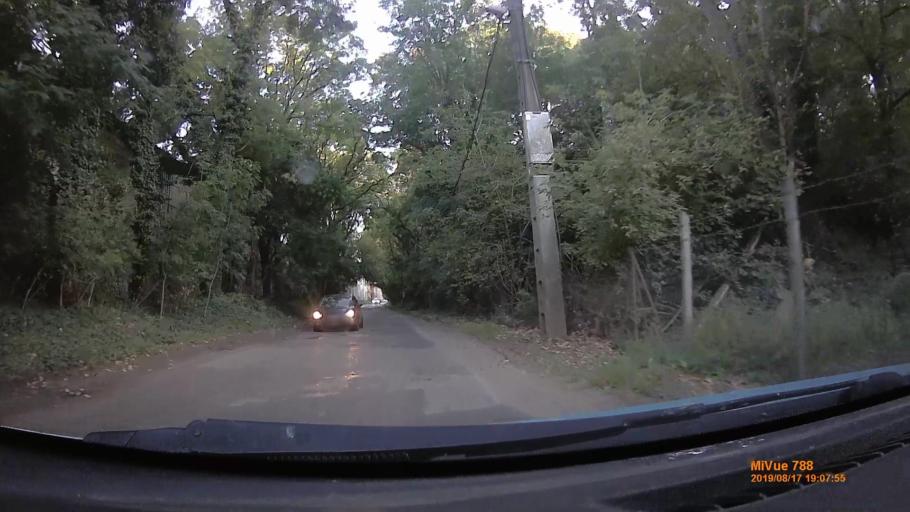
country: HU
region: Budapest
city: Budapest IV. keruelet
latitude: 47.5651
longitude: 19.0749
